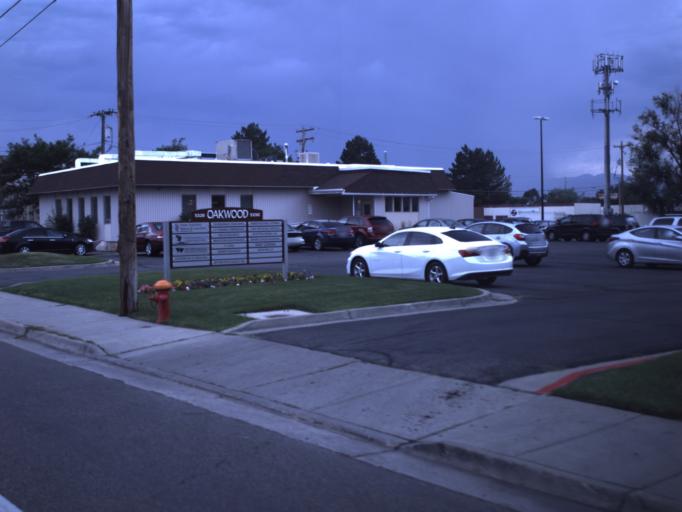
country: US
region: Utah
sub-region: Salt Lake County
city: Murray
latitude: 40.6546
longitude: -111.8660
